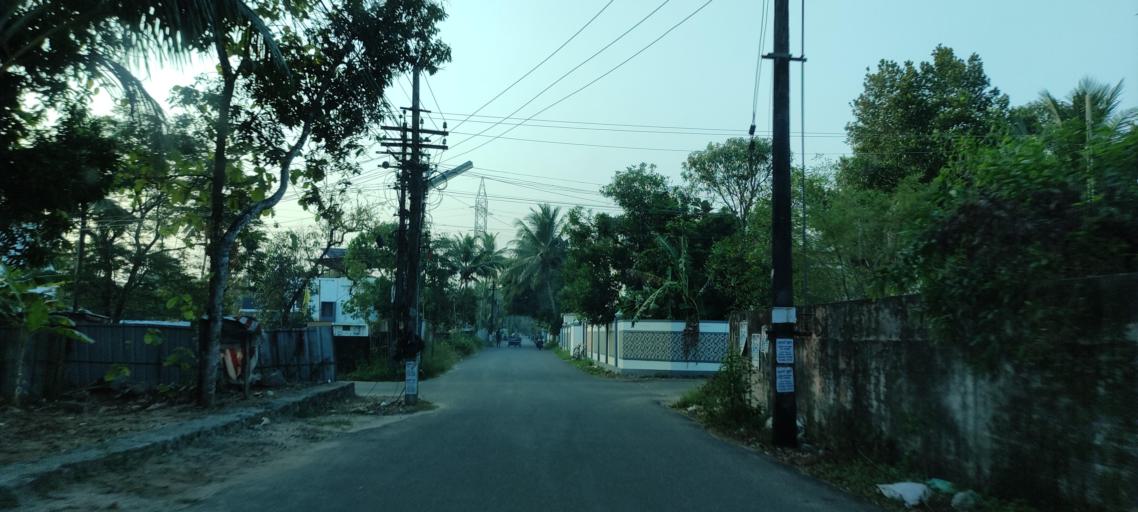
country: IN
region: Kerala
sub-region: Alappuzha
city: Alleppey
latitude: 9.4278
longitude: 76.3479
